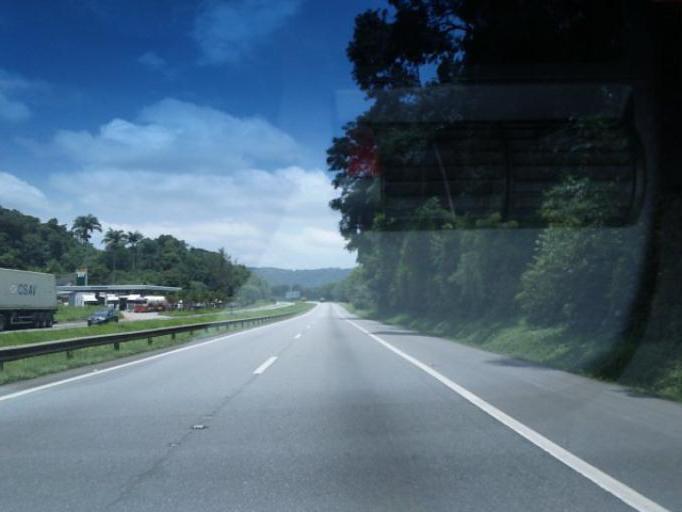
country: BR
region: Sao Paulo
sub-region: Miracatu
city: Miracatu
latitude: -24.1965
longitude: -47.3651
